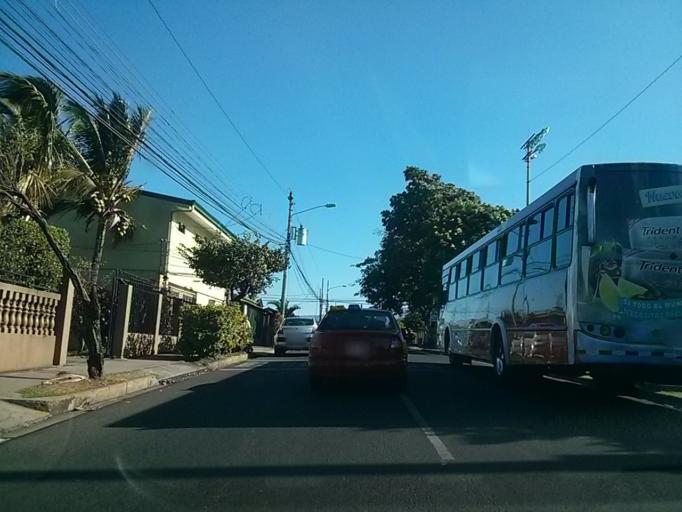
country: CR
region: Heredia
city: La Asuncion
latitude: 9.9801
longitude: -84.1707
